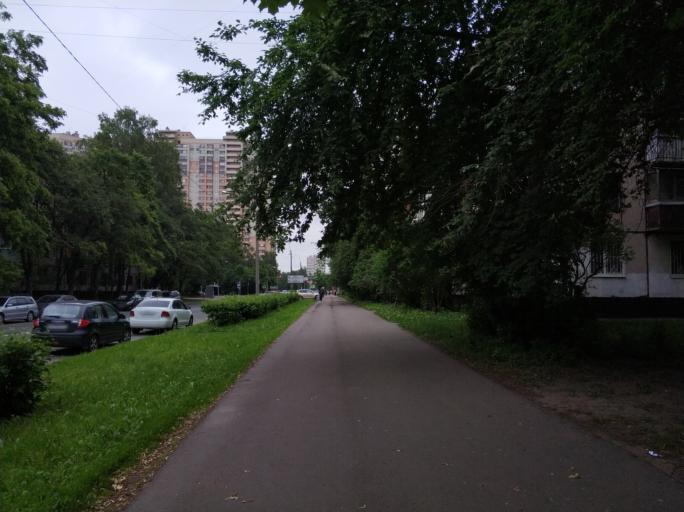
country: RU
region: St.-Petersburg
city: Grazhdanka
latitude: 60.0330
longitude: 30.3986
